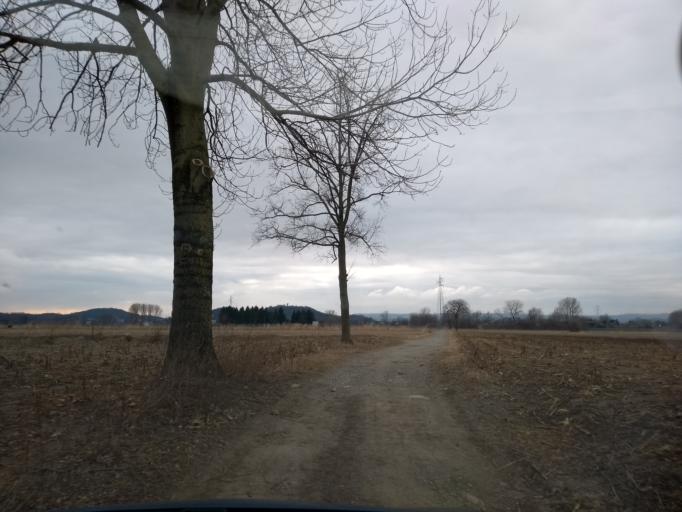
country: IT
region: Piedmont
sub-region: Provincia di Torino
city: Fiorano Canavese
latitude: 45.4796
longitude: 7.8429
